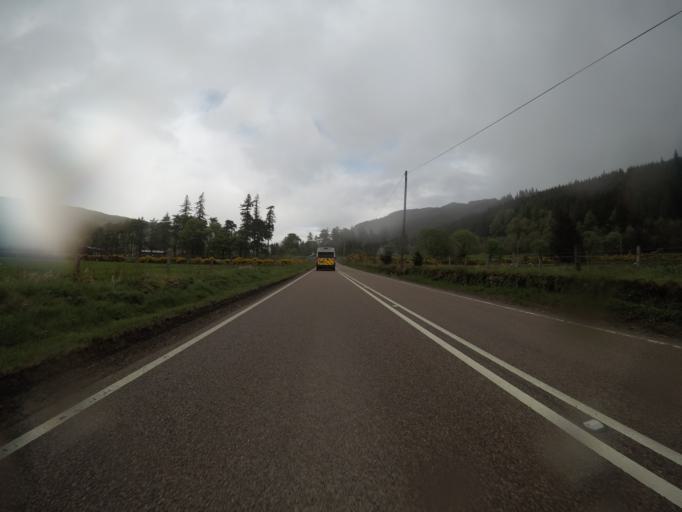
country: GB
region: Scotland
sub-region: Highland
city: Spean Bridge
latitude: 57.0320
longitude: -4.8151
